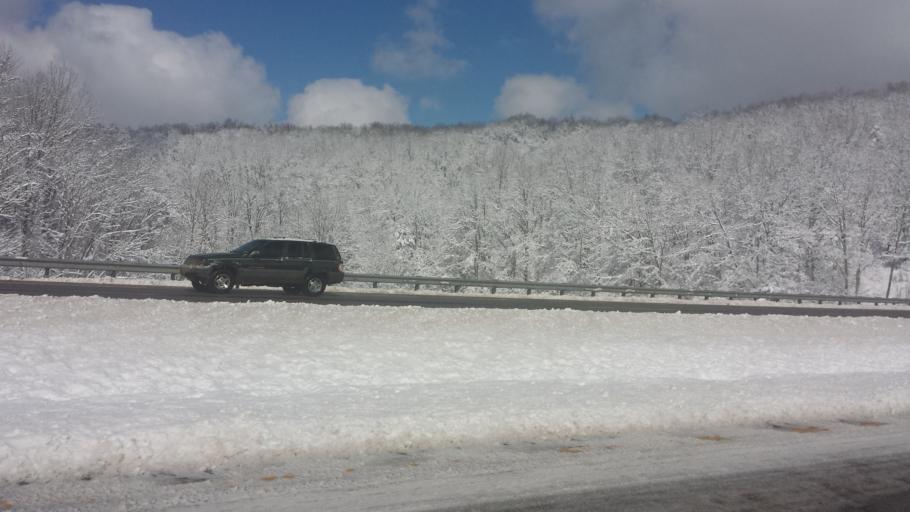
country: US
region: West Virginia
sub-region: Kanawha County
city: Sissonville
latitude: 38.6459
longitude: -81.6466
